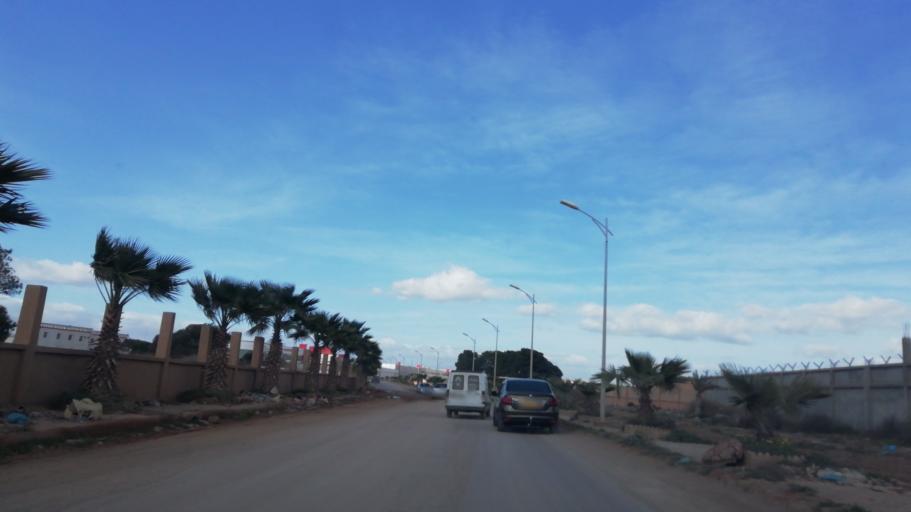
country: DZ
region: Oran
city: Es Senia
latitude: 35.6351
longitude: -0.5850
